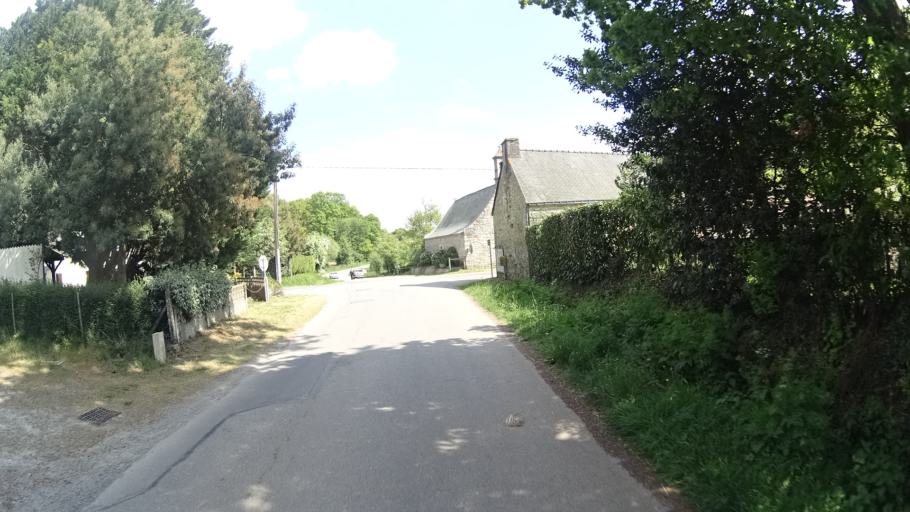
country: FR
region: Brittany
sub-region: Departement du Morbihan
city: Allaire
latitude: 47.5988
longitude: -2.1593
